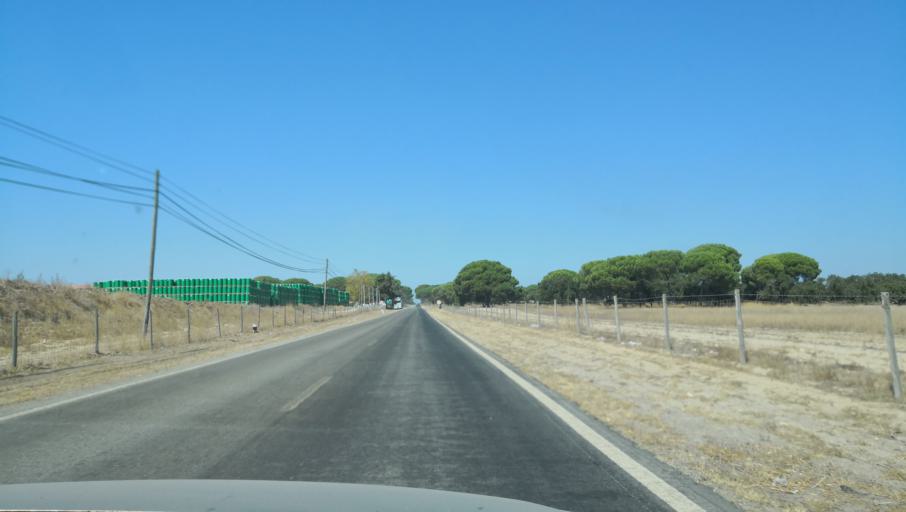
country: PT
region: Setubal
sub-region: Alcacer do Sal
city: Alcacer do Sal
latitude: 38.3707
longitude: -8.5490
